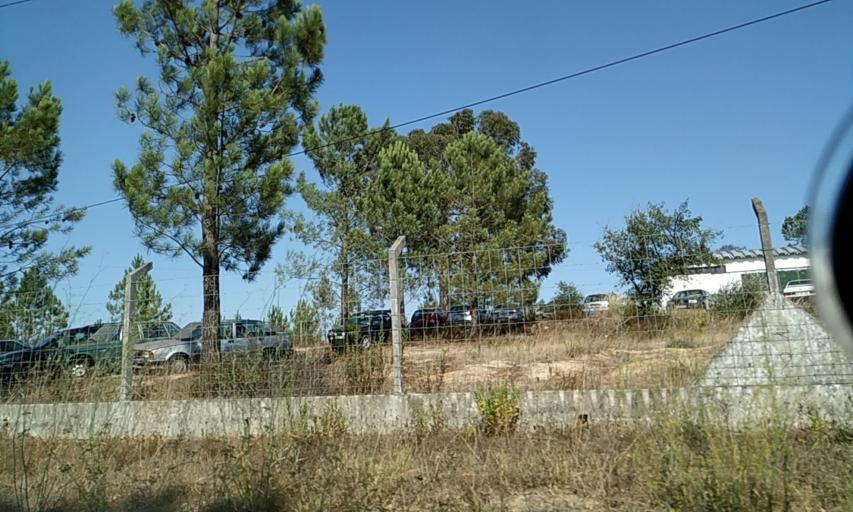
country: PT
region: Santarem
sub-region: Benavente
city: Poceirao
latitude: 38.7593
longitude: -8.6324
